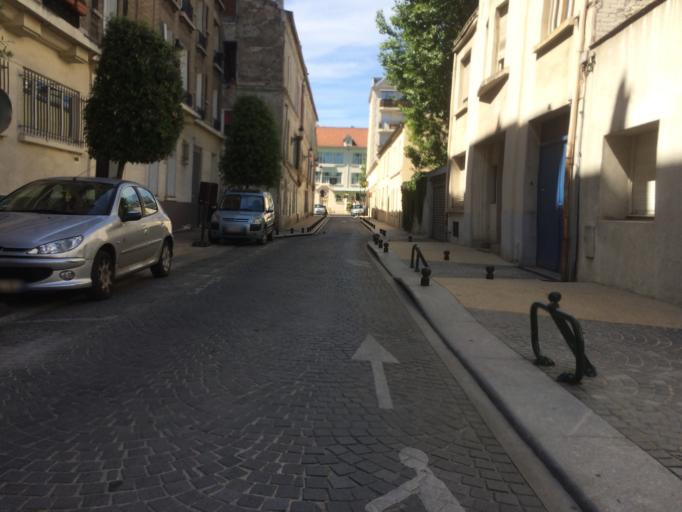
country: FR
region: Ile-de-France
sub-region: Departement des Hauts-de-Seine
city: Puteaux
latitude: 48.8811
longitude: 2.2401
